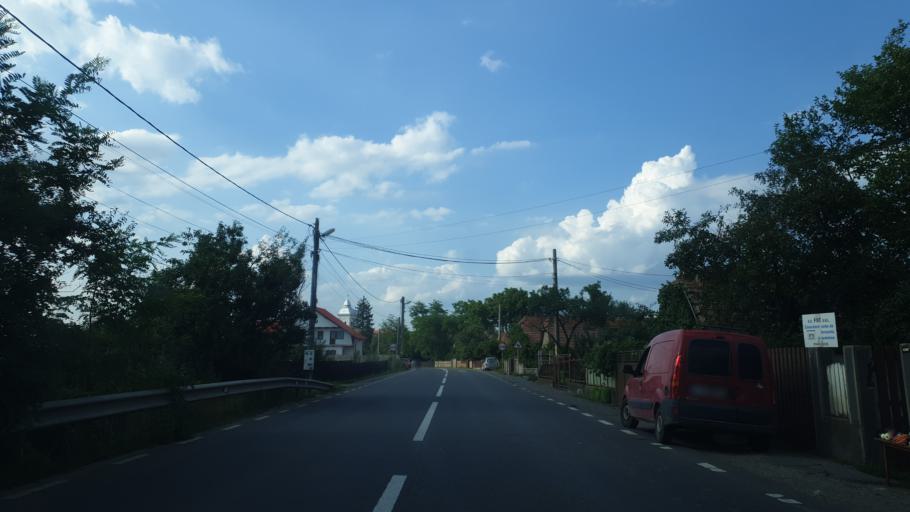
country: RO
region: Covasna
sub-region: Comuna Chichis
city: Chichis
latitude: 45.8105
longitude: 25.8003
